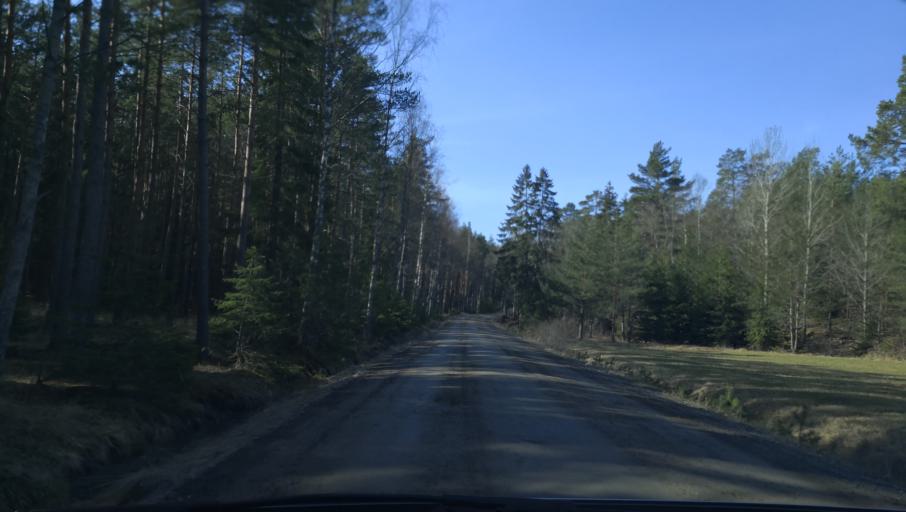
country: SE
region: Stockholm
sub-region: Varmdo Kommun
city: Gustavsberg
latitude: 59.2943
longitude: 18.3859
